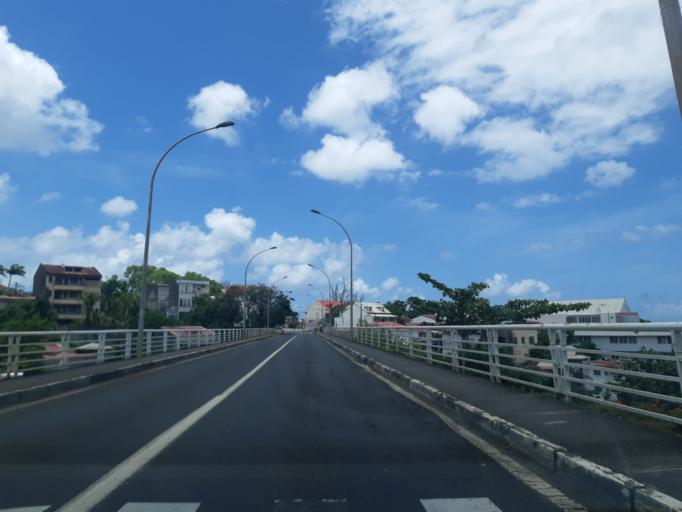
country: GP
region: Guadeloupe
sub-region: Guadeloupe
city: Basse-Terre
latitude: 15.9964
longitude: -61.7272
